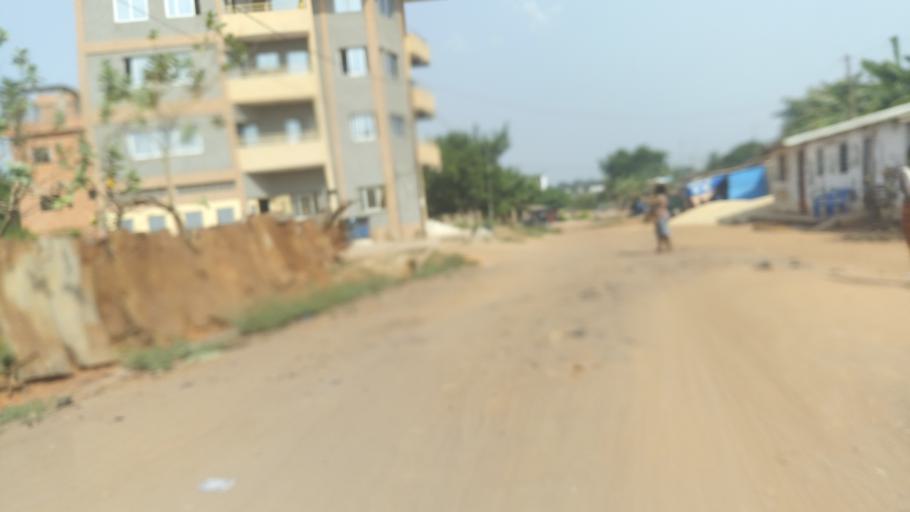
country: TG
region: Maritime
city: Lome
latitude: 6.1680
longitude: 1.2058
